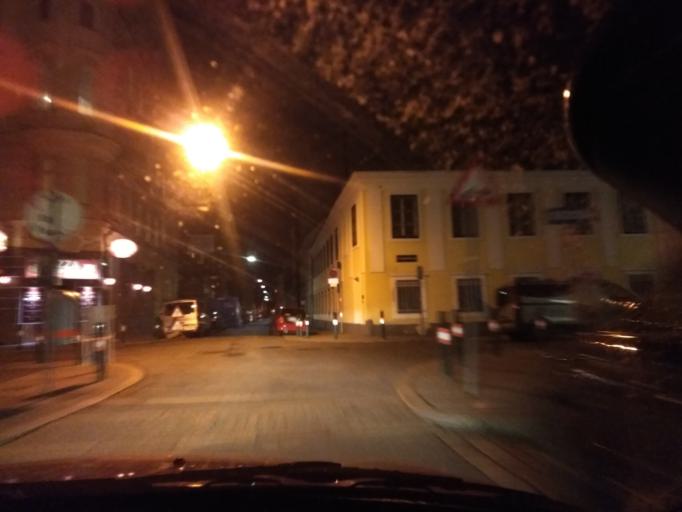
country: AT
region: Vienna
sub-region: Wien Stadt
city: Vienna
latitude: 48.1894
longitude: 16.3591
